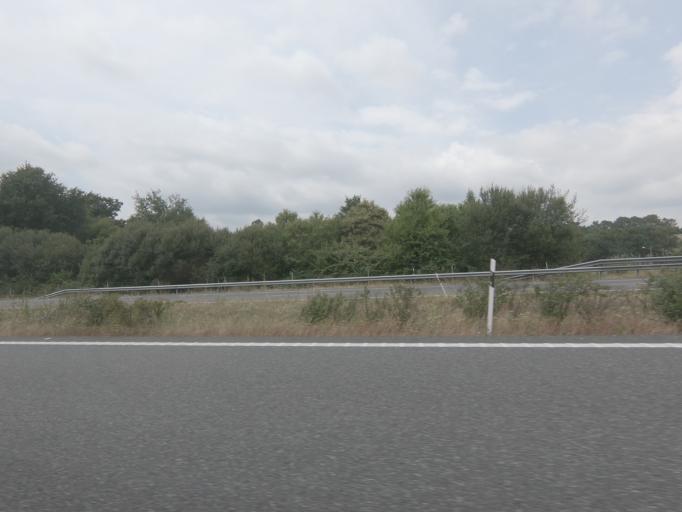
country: ES
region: Galicia
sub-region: Provincia de Pontevedra
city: Ponteareas
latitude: 42.1549
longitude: -8.4910
